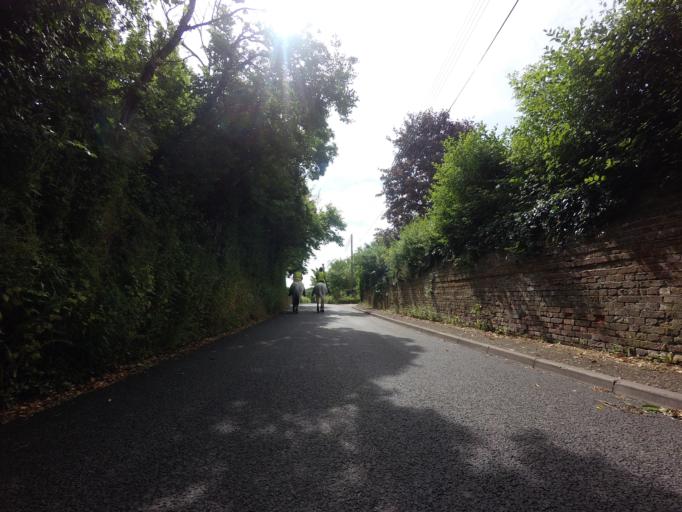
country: GB
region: England
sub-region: Kent
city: Halstead
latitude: 51.3560
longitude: 0.1337
